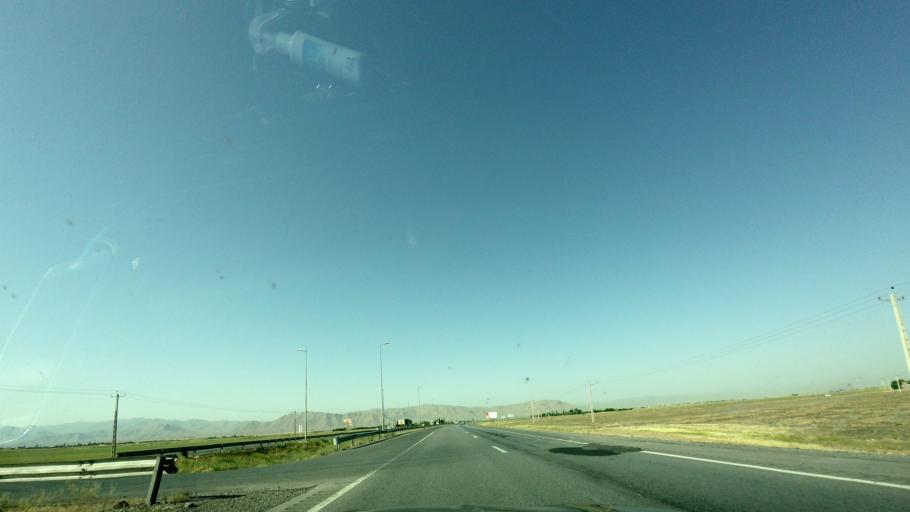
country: IR
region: Markazi
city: Ashtian
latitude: 34.1901
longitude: 50.0538
